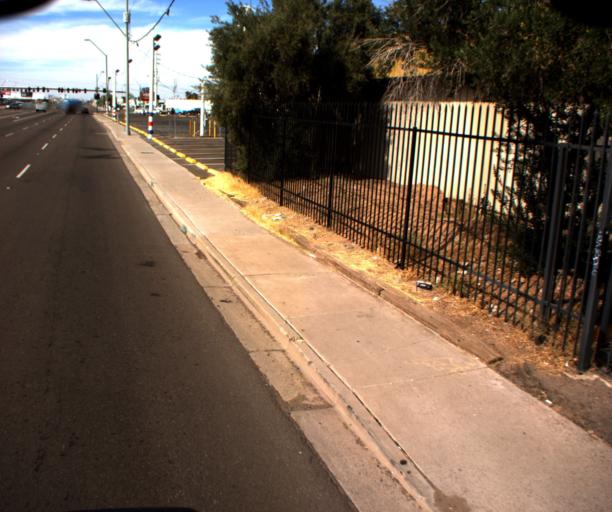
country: US
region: Arizona
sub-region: Maricopa County
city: Phoenix
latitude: 33.4647
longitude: -112.0984
